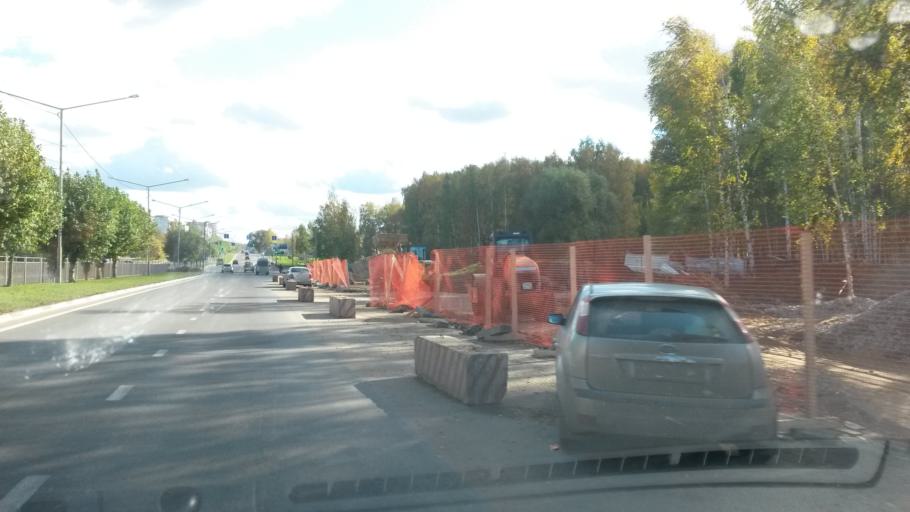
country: RU
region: Jaroslavl
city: Yaroslavl
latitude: 57.5765
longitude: 39.9165
